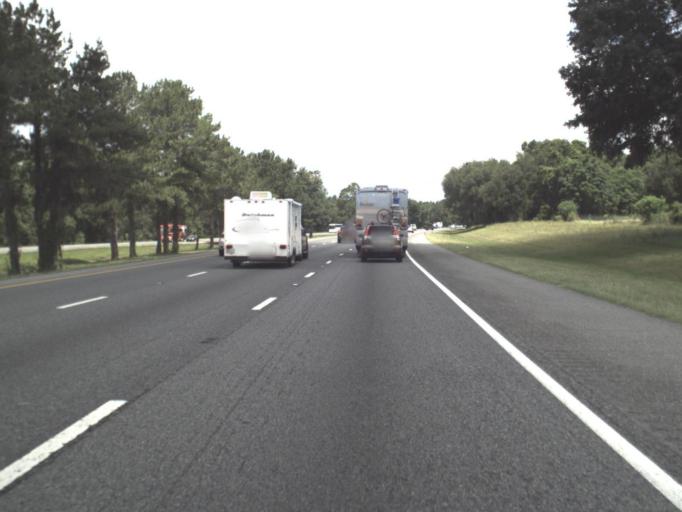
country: US
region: Florida
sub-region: Suwannee County
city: Wellborn
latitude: 30.2395
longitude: -82.7378
